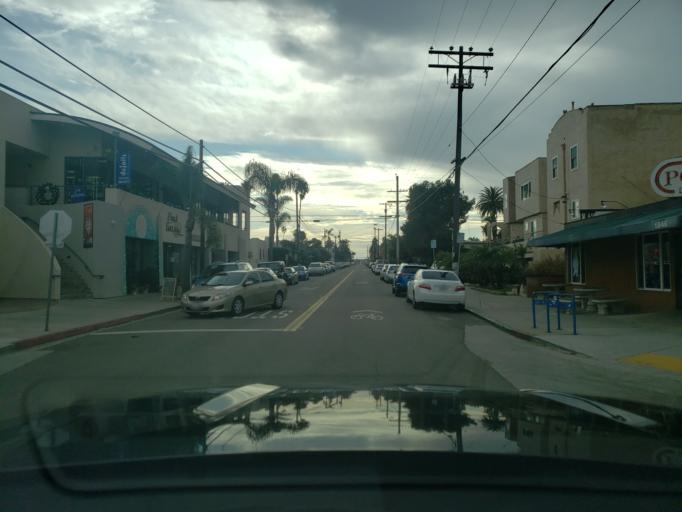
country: US
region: California
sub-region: San Diego County
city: Coronado
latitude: 32.7460
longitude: -117.2519
